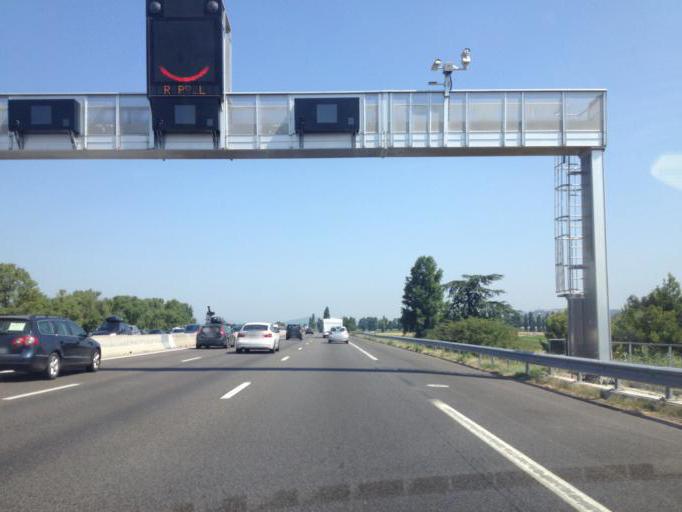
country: FR
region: Rhone-Alpes
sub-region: Departement de la Drome
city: Saint-Paul-Trois-Chateaux
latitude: 44.3533
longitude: 4.7379
